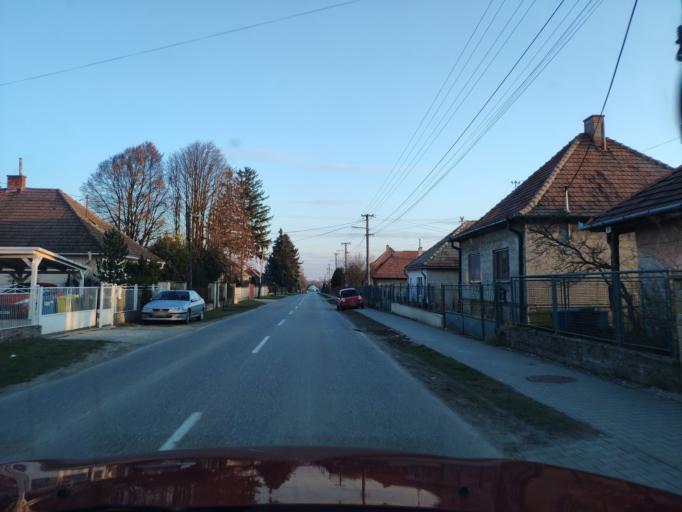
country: SK
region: Nitriansky
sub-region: Okres Nitra
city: Nitra
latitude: 48.2160
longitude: 18.0568
